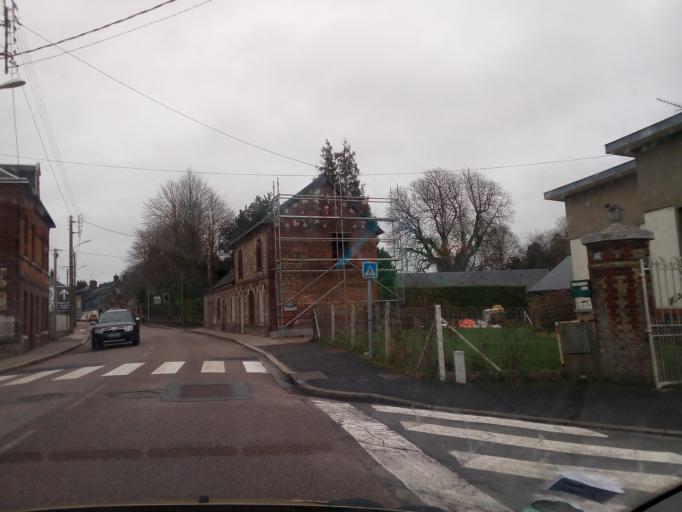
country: FR
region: Haute-Normandie
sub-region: Departement de la Seine-Maritime
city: Yvetot
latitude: 49.6126
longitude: 0.7502
